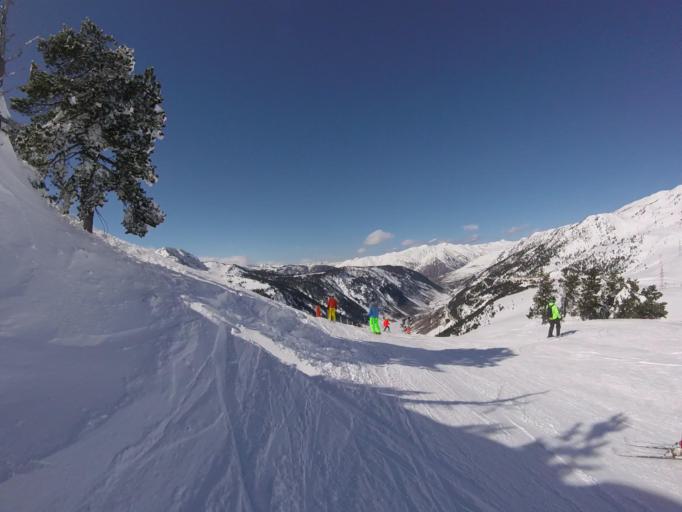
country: ES
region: Catalonia
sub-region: Provincia de Lleida
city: Espot
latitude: 42.6582
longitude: 0.9807
